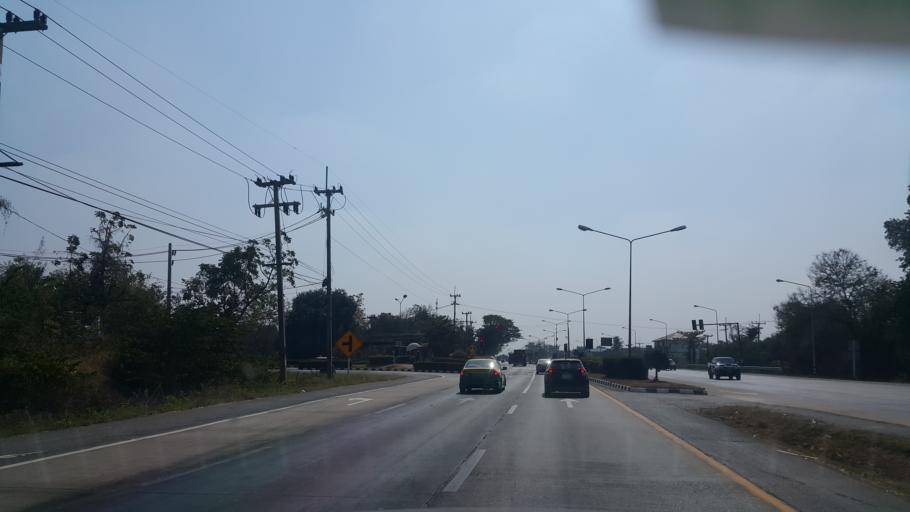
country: TH
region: Nakhon Ratchasima
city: Non Daeng
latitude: 15.3492
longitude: 102.4463
